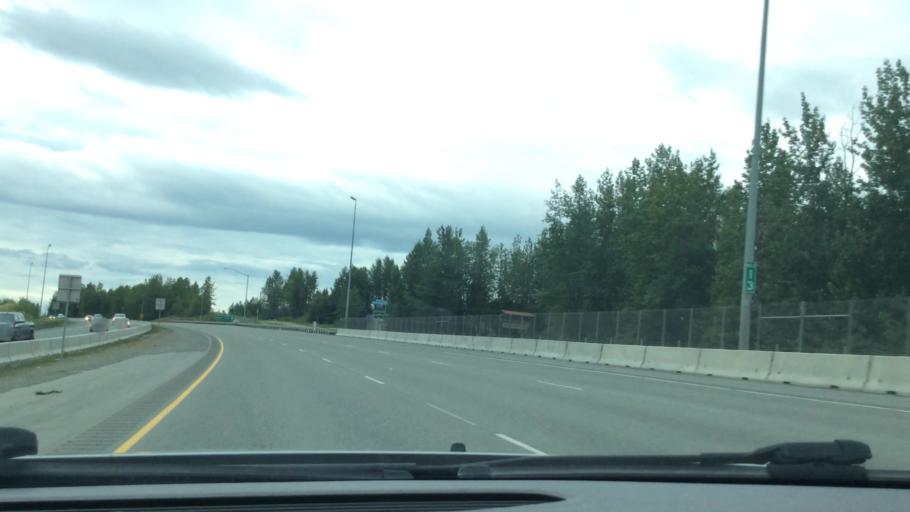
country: US
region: Alaska
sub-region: Anchorage Municipality
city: Eagle River
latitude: 61.3131
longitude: -149.5754
